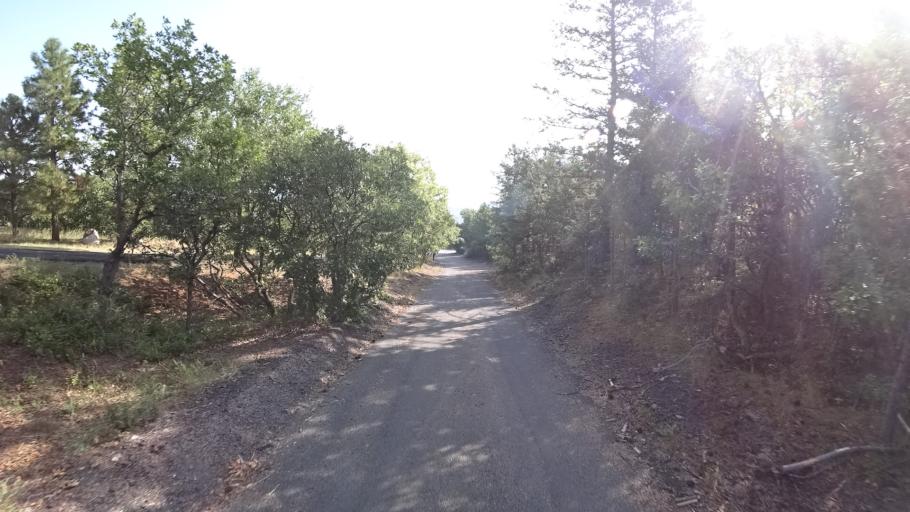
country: US
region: Colorado
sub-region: El Paso County
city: Colorado Springs
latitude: 38.8101
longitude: -104.8761
